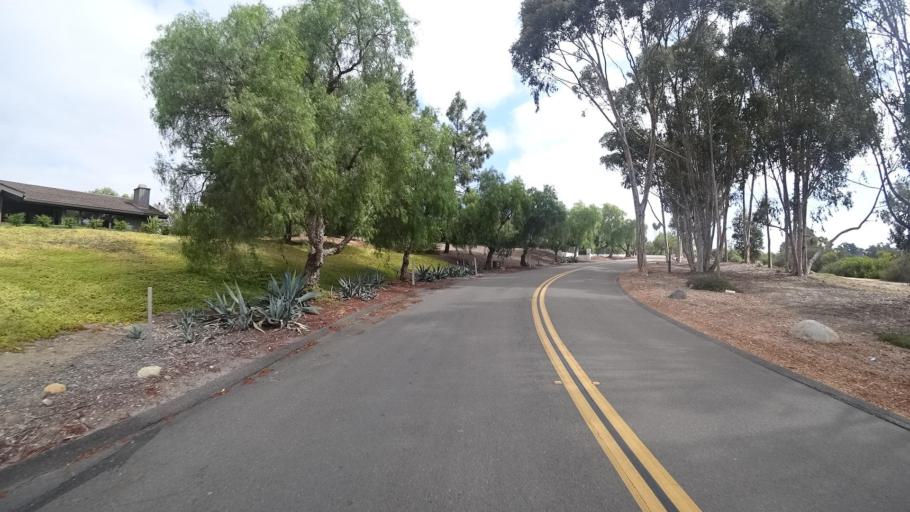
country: US
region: California
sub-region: San Diego County
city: Rancho Santa Fe
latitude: 33.0241
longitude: -117.2261
